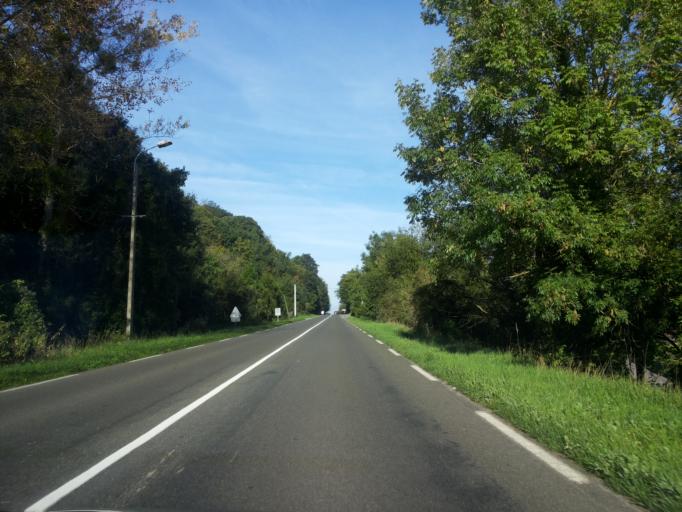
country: FR
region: Picardie
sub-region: Departement de l'Aisne
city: Crepy
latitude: 49.6172
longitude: 3.4628
